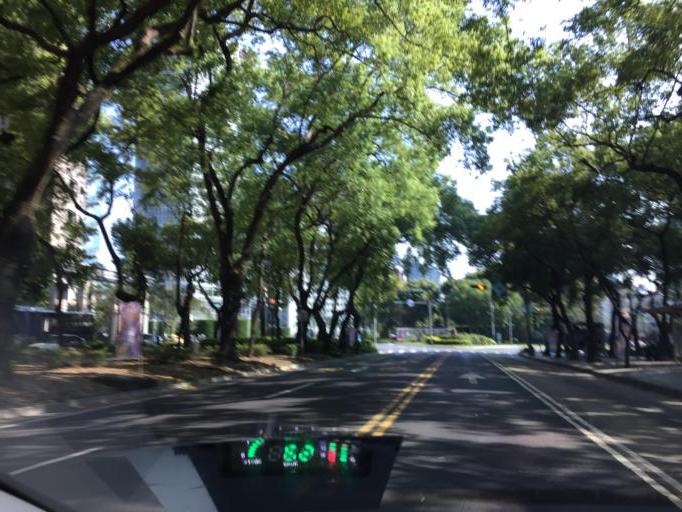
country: TW
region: Taipei
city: Taipei
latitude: 25.0396
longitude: 121.5489
